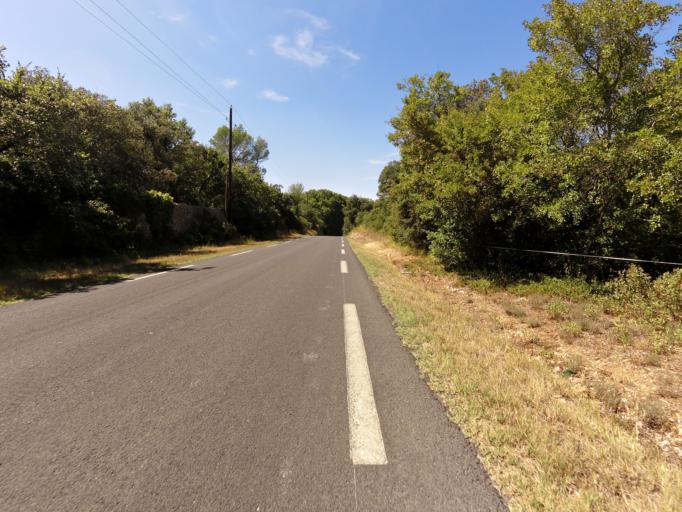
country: FR
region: Languedoc-Roussillon
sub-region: Departement de l'Herault
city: Boisseron
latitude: 43.7612
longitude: 4.1046
